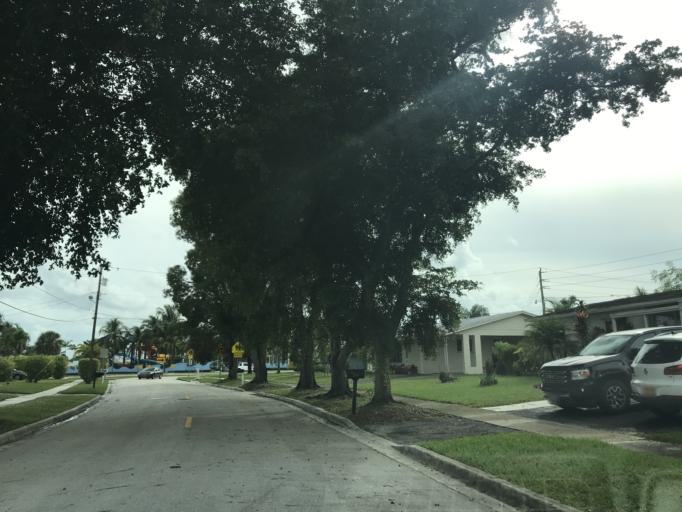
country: US
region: Florida
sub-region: Broward County
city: Margate
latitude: 26.2552
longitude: -80.2097
